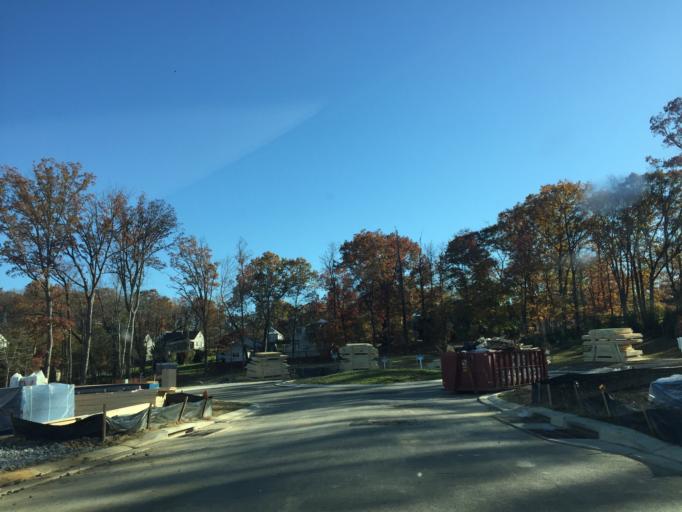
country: US
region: Maryland
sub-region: Baltimore County
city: Parkville
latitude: 39.4041
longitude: -76.5516
